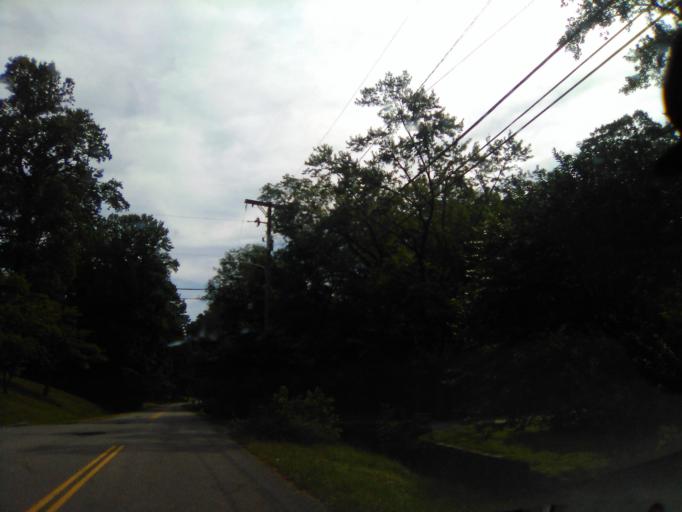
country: US
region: Tennessee
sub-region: Davidson County
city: Belle Meade
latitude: 36.0979
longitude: -86.9117
